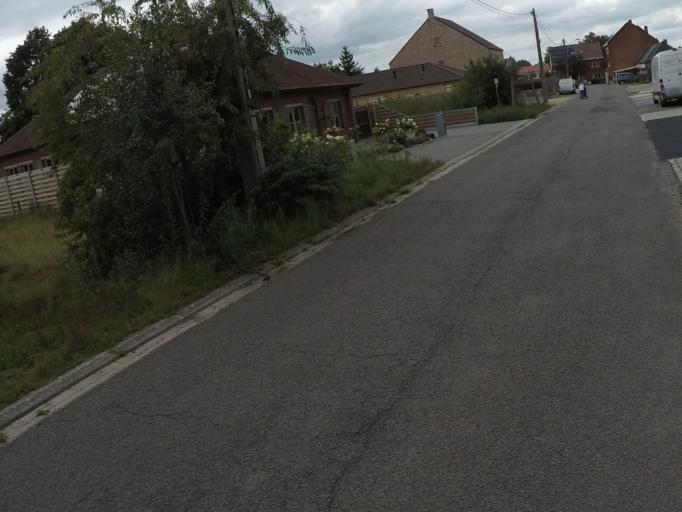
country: BE
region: Flanders
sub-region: Provincie Antwerpen
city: Grobbendonk
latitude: 51.2044
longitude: 4.7164
